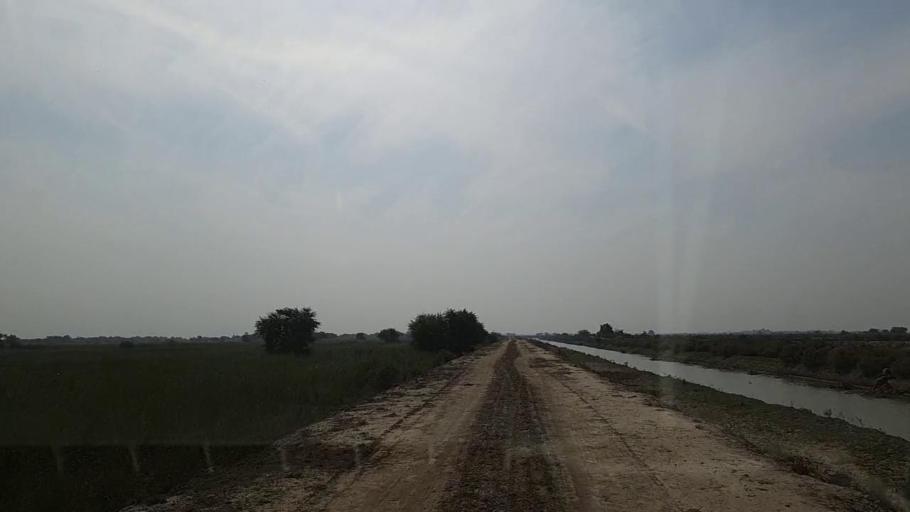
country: PK
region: Sindh
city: Mirpur Batoro
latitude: 24.6692
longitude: 68.2500
